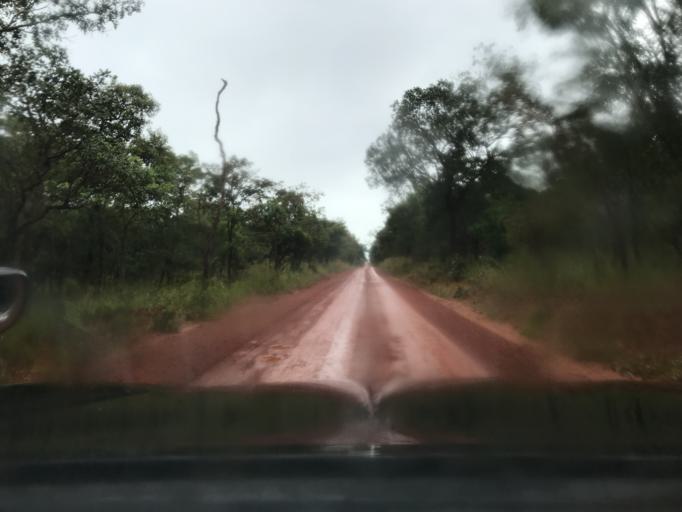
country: TZ
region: Kigoma
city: Uvinza
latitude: -5.2952
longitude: 30.3721
